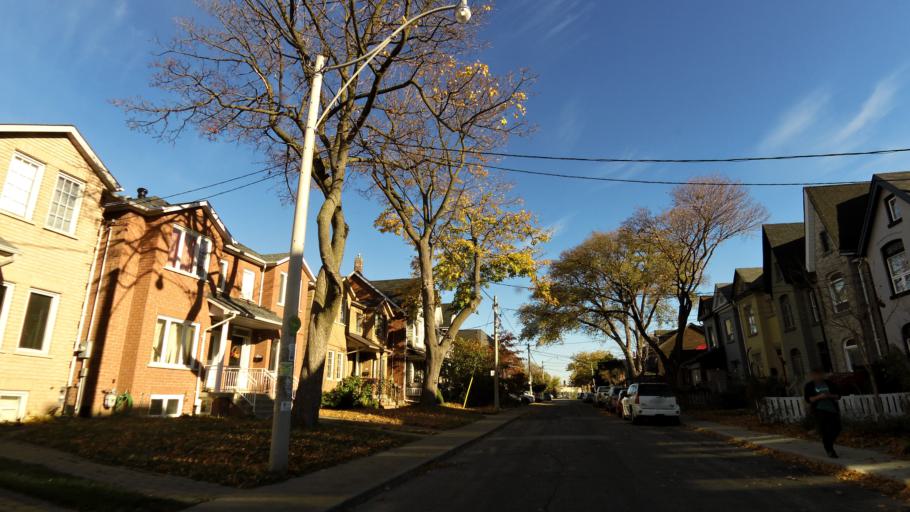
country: CA
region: Ontario
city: Toronto
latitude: 43.6660
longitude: -79.4612
